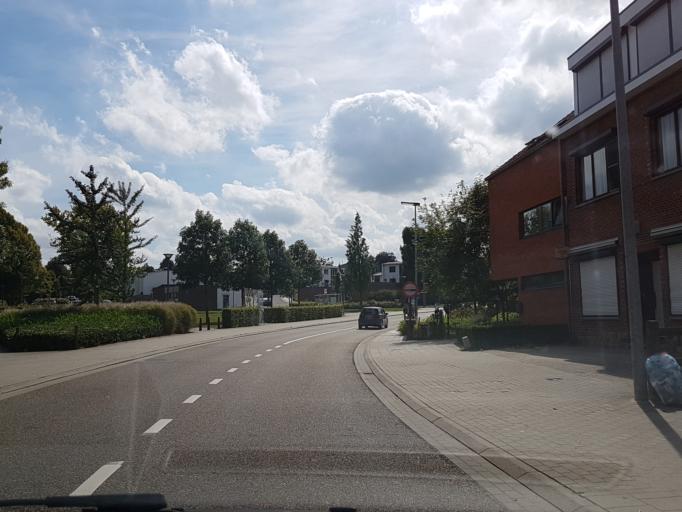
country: BE
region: Flanders
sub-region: Provincie Vlaams-Brabant
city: Oud-Heverlee
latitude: 50.8623
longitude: 4.6595
